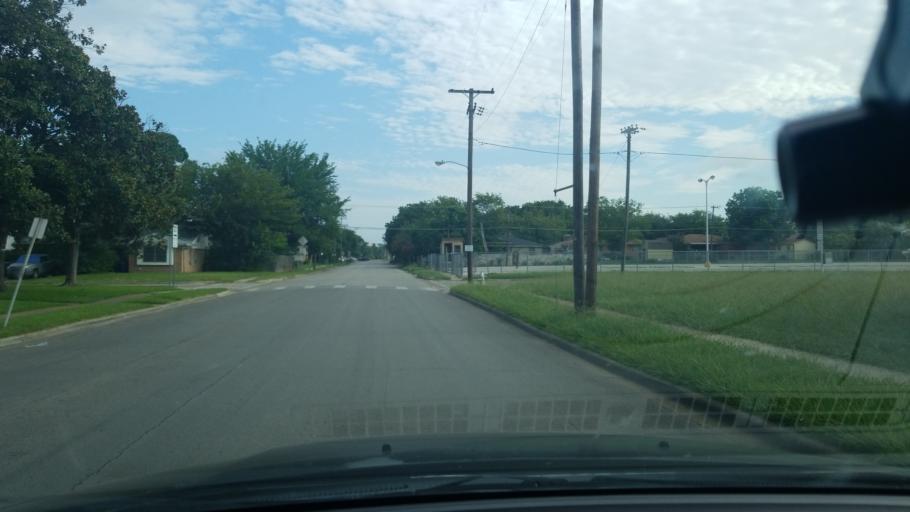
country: US
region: Texas
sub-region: Dallas County
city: Balch Springs
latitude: 32.7464
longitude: -96.6698
